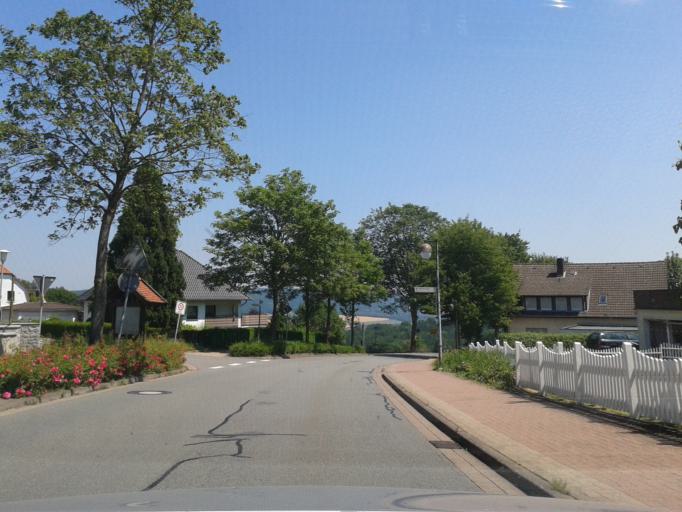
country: DE
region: North Rhine-Westphalia
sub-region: Regierungsbezirk Detmold
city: Lugde
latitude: 51.9761
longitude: 9.1944
